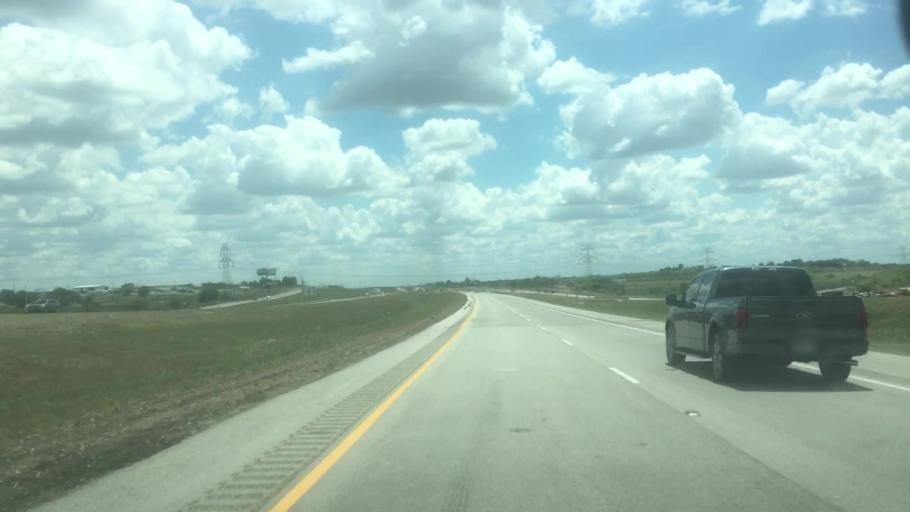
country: US
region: Texas
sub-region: Caldwell County
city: Uhland
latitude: 30.0009
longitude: -97.6869
